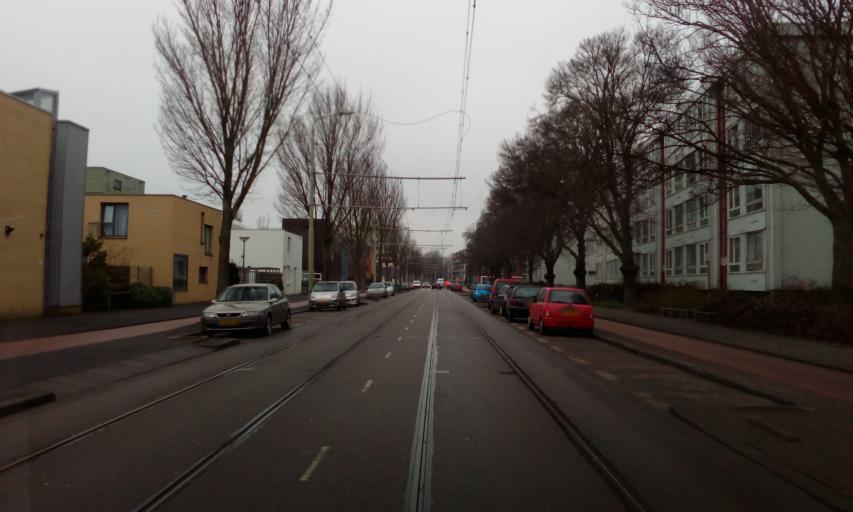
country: NL
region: South Holland
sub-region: Gemeente Westland
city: Kwintsheul
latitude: 52.0481
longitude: 4.2668
